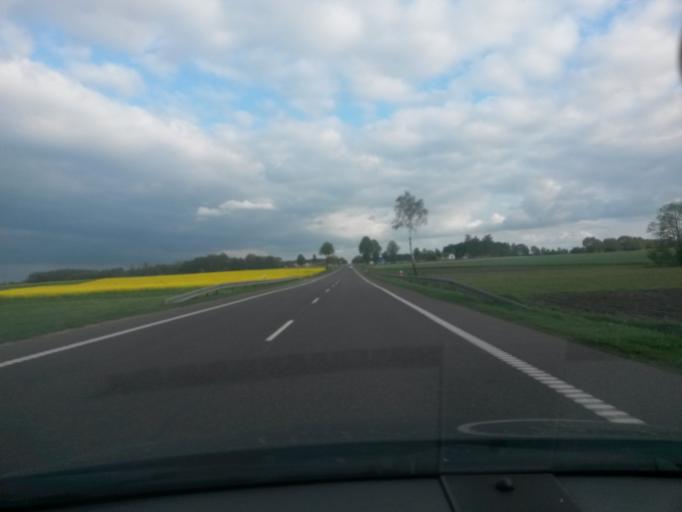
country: PL
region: Masovian Voivodeship
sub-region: Powiat plocki
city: Starozreby
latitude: 52.6786
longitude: 20.0618
